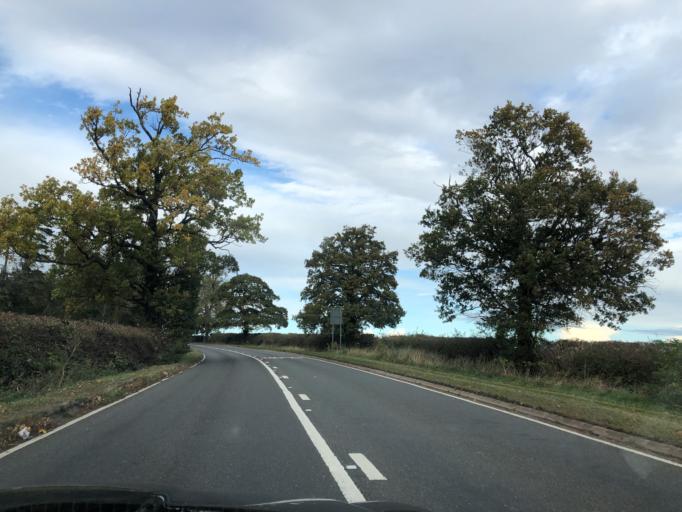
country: GB
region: England
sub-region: Warwickshire
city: Warwick
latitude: 52.2500
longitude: -1.5589
